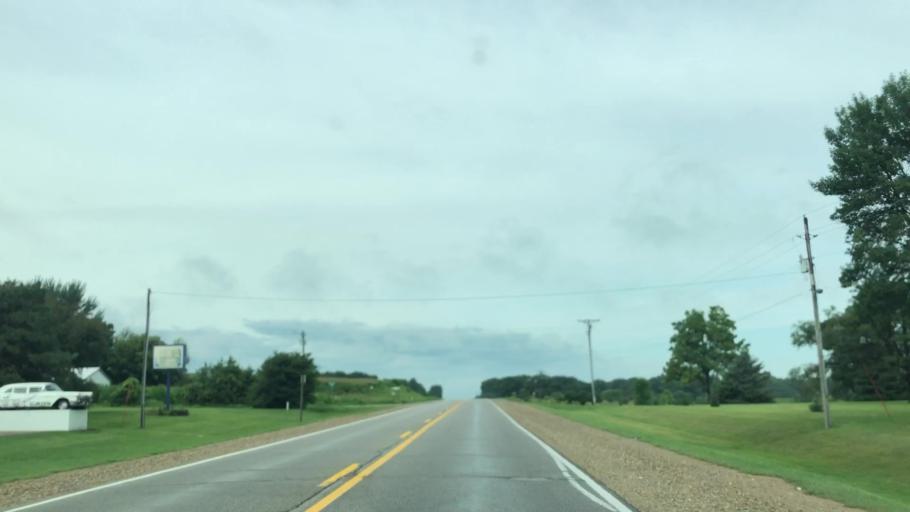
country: US
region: Iowa
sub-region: Marshall County
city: Marshalltown
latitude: 42.0075
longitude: -92.9403
